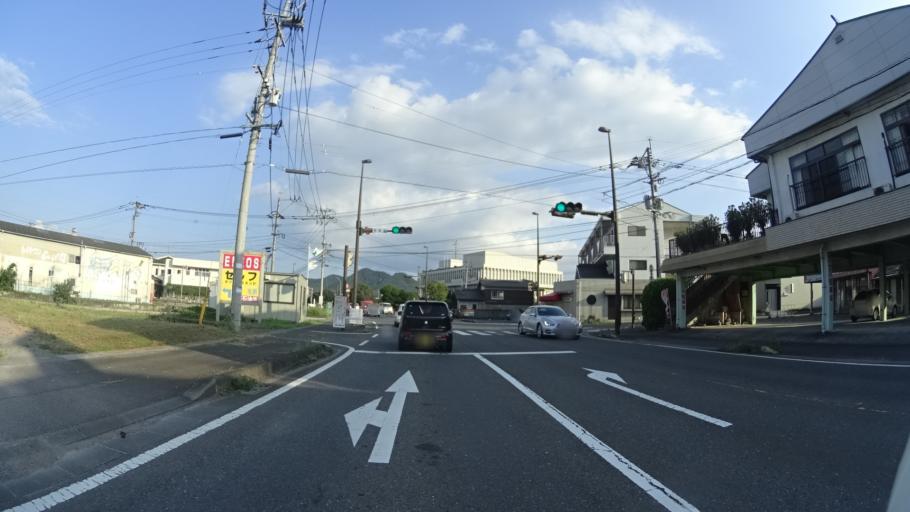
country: JP
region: Oita
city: Bungo-Takada-shi
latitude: 33.4399
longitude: 131.3533
